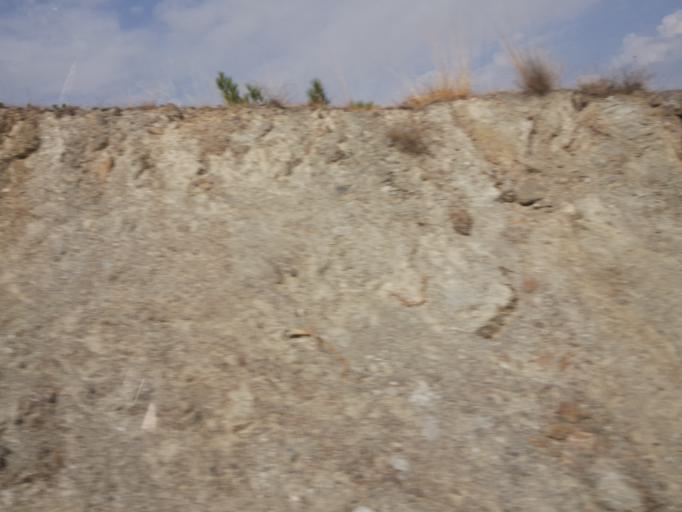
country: TR
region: Corum
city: Kamil
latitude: 41.1096
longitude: 34.7407
